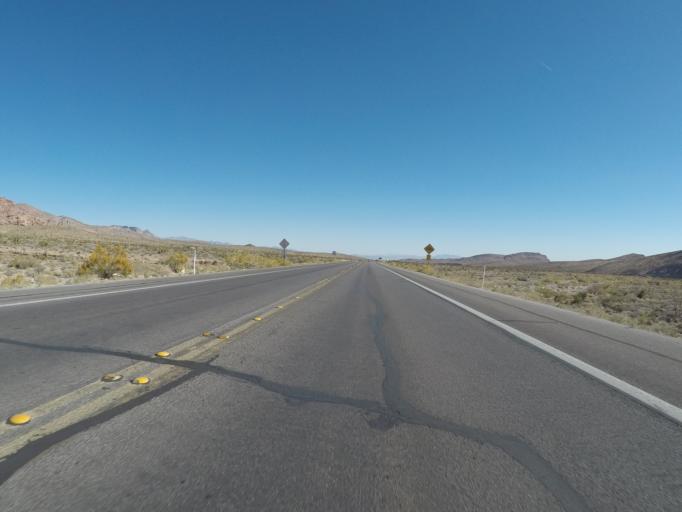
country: US
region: Nevada
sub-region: Clark County
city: Summerlin South
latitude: 36.1291
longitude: -115.4269
